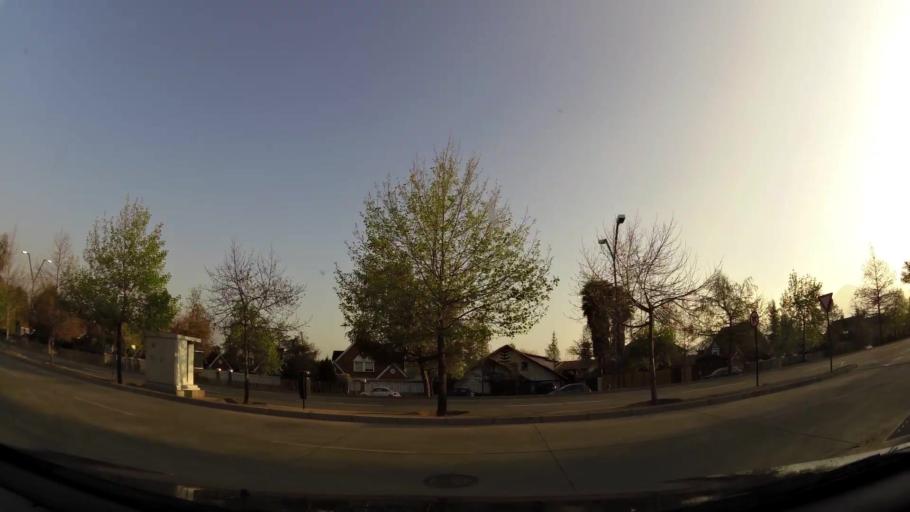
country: CL
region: Santiago Metropolitan
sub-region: Provincia de Chacabuco
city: Chicureo Abajo
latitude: -33.3262
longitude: -70.5153
